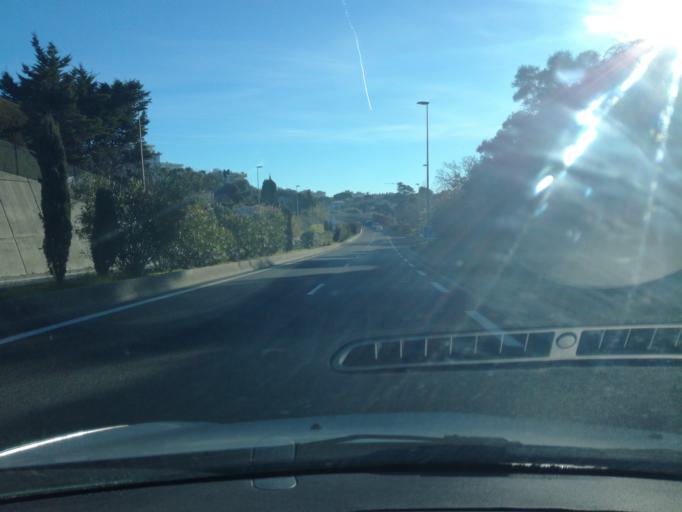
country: FR
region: Provence-Alpes-Cote d'Azur
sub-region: Departement des Alpes-Maritimes
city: Antibes
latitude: 43.5786
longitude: 7.0992
